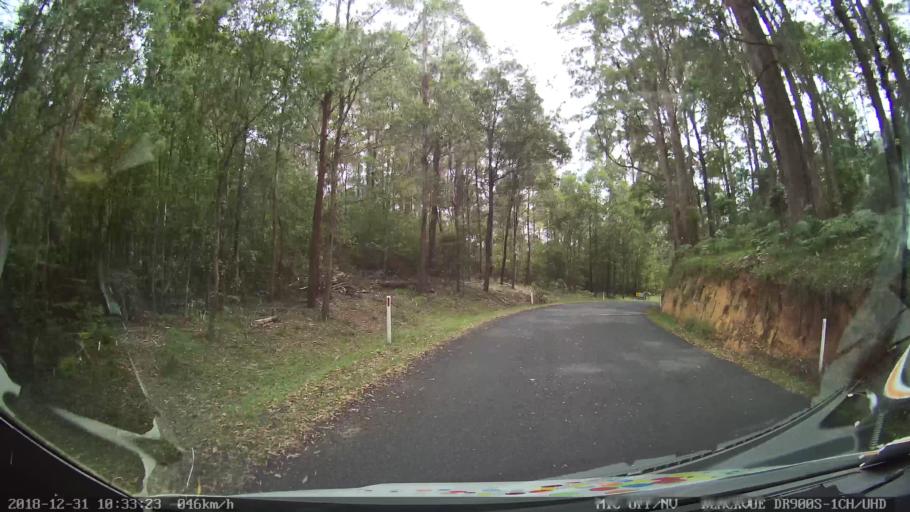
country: AU
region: New South Wales
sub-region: Snowy River
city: Jindabyne
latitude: -36.4470
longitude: 148.1638
